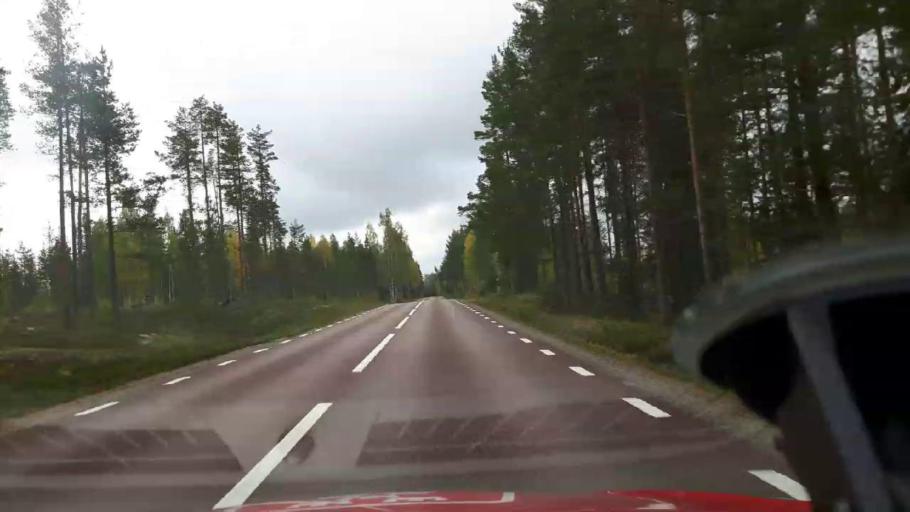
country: SE
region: Jaemtland
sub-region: Harjedalens Kommun
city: Sveg
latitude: 62.2046
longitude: 14.8492
